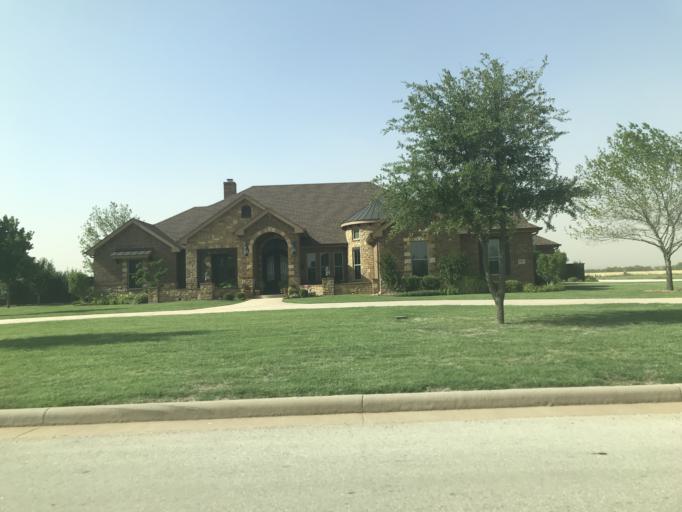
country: US
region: Texas
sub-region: Taylor County
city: Potosi
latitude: 32.3499
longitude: -99.7136
